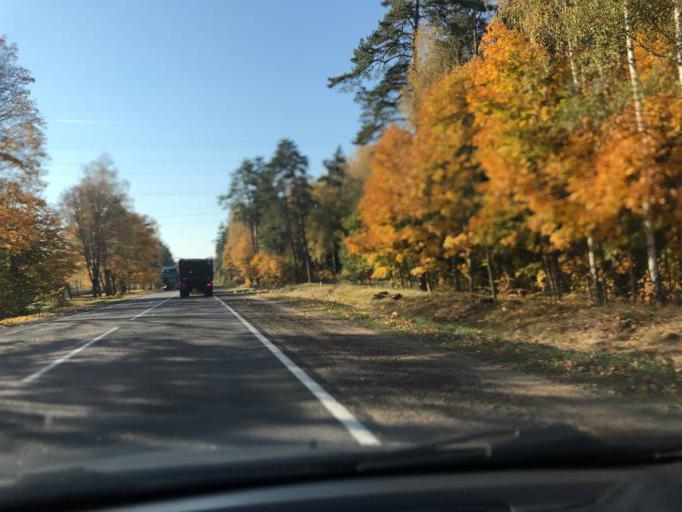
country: BY
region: Mogilev
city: Hlusha
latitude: 53.0884
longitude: 28.8725
